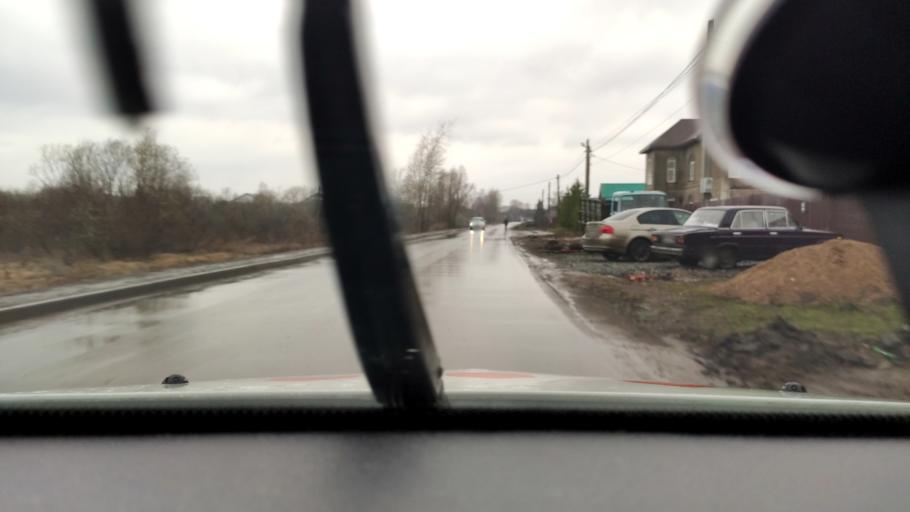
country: RU
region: Bashkortostan
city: Mikhaylovka
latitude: 54.7841
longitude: 55.8179
